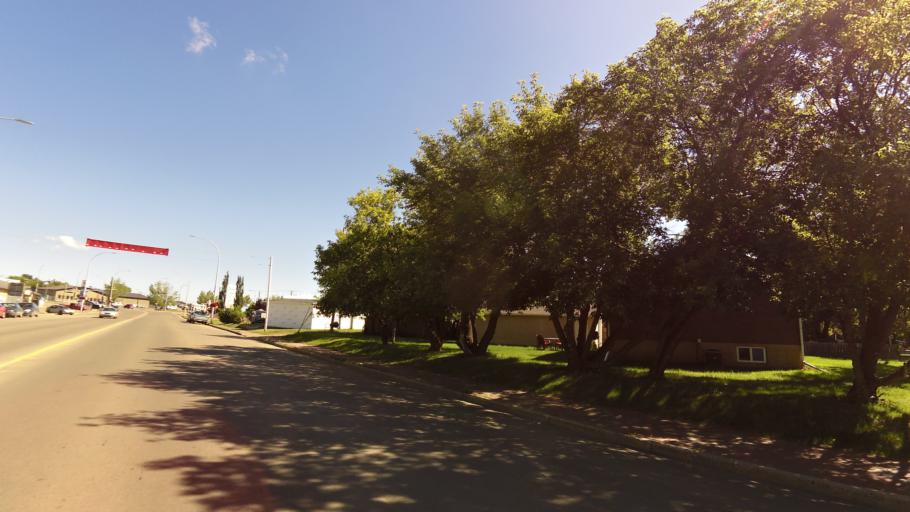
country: CA
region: Alberta
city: Wainwright
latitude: 52.8415
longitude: -110.8522
